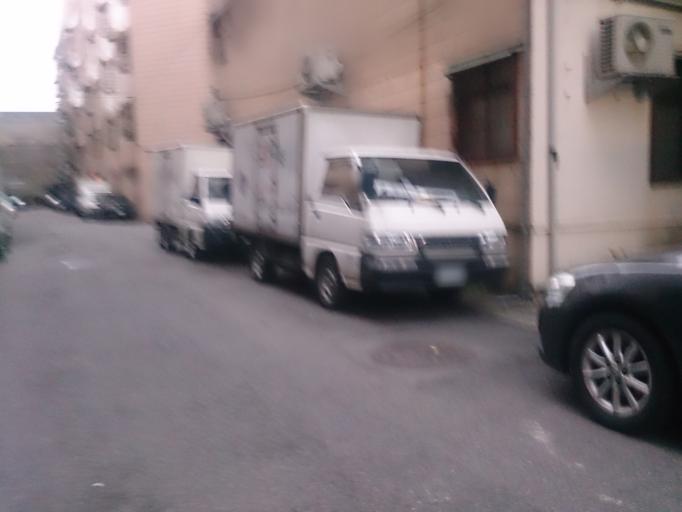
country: TW
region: Taipei
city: Taipei
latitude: 25.0565
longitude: 121.5847
